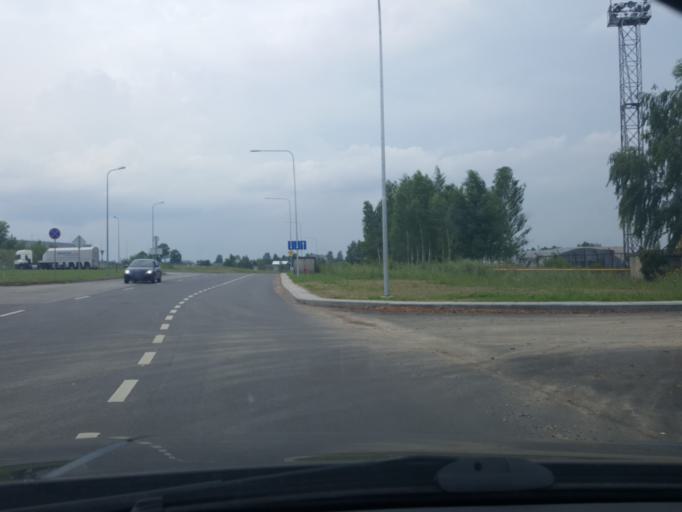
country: LT
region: Alytaus apskritis
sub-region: Alytus
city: Alytus
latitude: 54.4378
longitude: 24.0117
